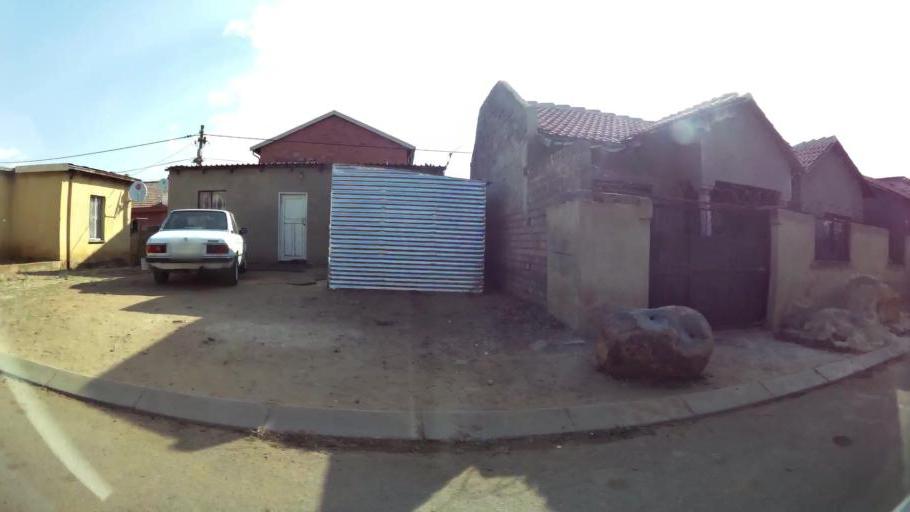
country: ZA
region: Gauteng
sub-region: City of Johannesburg Metropolitan Municipality
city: Soweto
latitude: -26.2577
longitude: 27.8948
